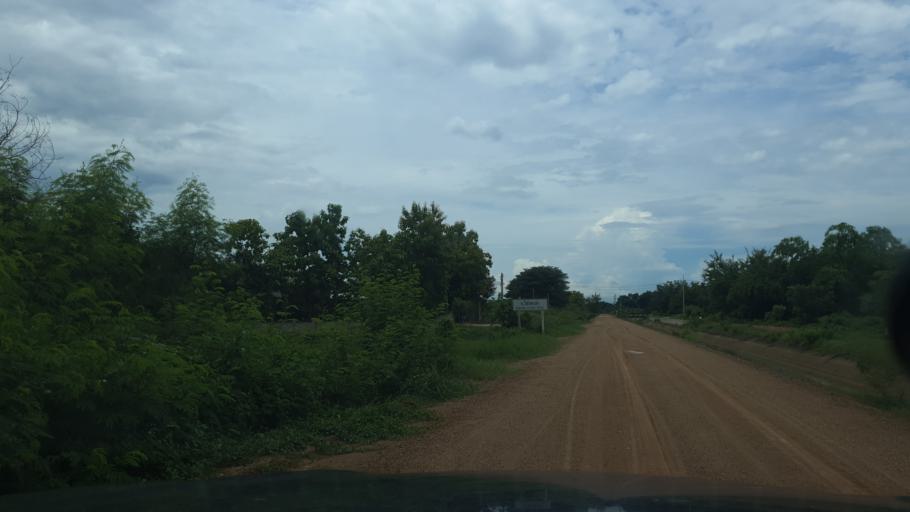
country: TH
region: Lampang
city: Hang Chat
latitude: 18.2946
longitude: 99.3714
